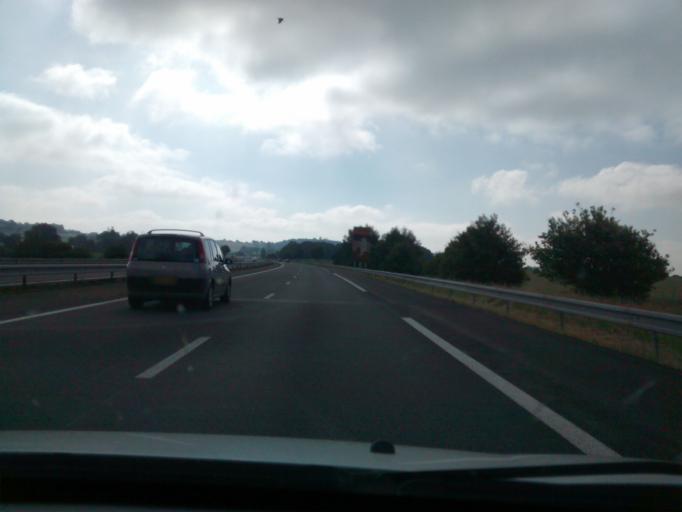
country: FR
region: Pays de la Loire
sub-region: Departement de la Sarthe
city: Brulon
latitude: 48.0074
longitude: -0.2844
